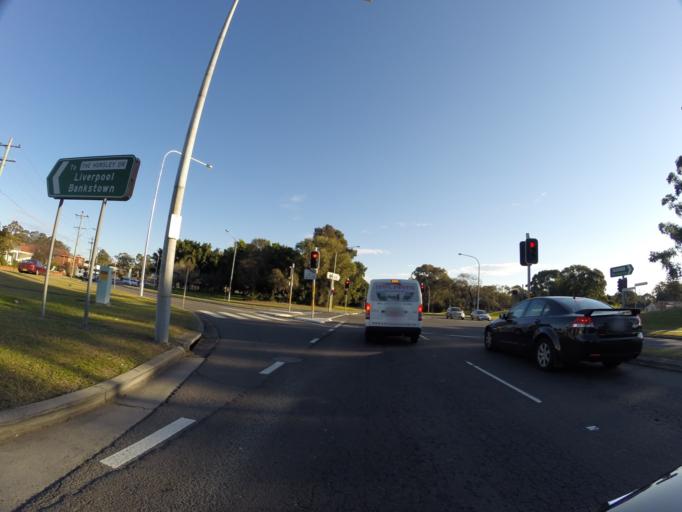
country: AU
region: New South Wales
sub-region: Fairfield
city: Fairfield East
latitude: -33.8696
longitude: 150.9632
